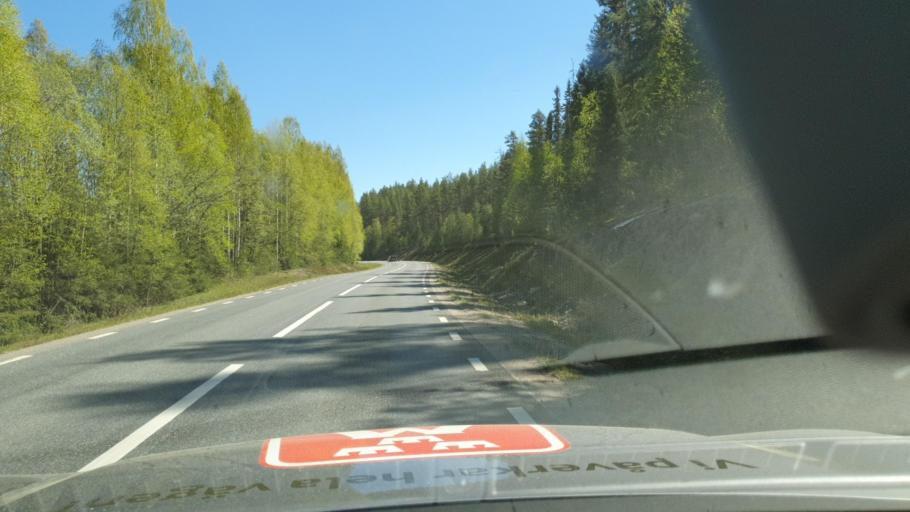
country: SE
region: Vaesternorrland
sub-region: OErnskoeldsviks Kommun
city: Bredbyn
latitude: 63.8034
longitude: 18.4914
